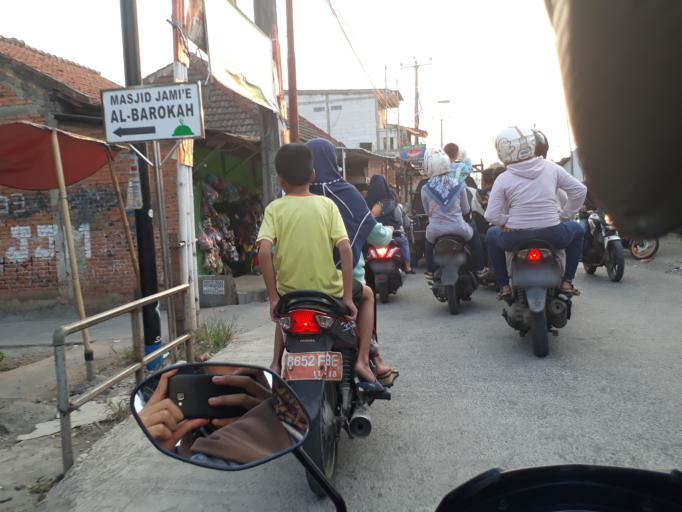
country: ID
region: West Java
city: Bekasi
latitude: -6.2432
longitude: 107.0438
